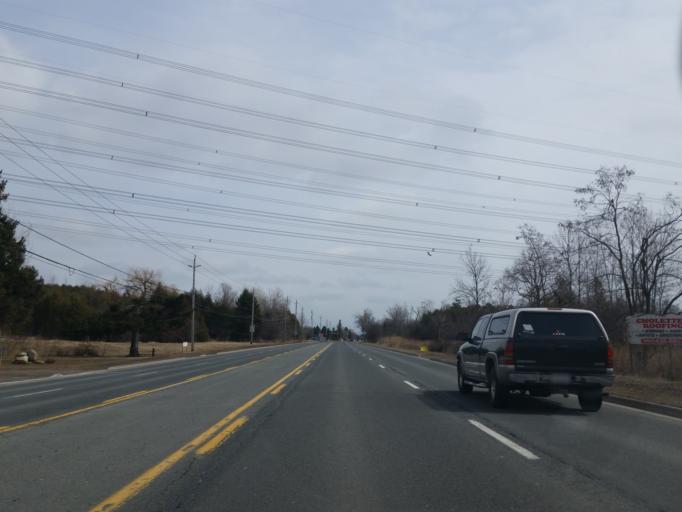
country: CA
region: Ontario
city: Oshawa
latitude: 43.9135
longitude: -78.7418
